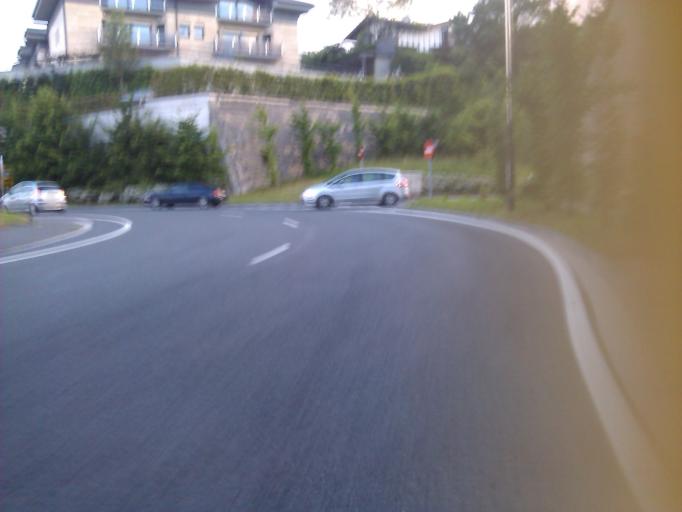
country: ES
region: Basque Country
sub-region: Provincia de Guipuzcoa
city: Irun
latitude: 43.3440
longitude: -1.7888
